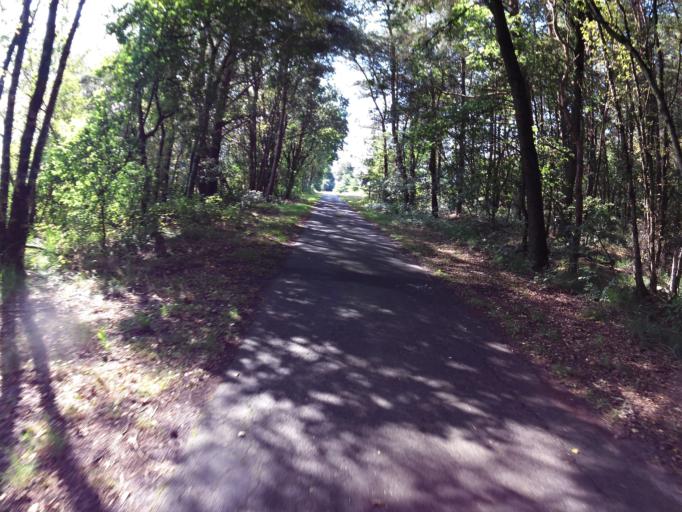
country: DE
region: Lower Saxony
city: Sandbostel
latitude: 53.3931
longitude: 9.1209
